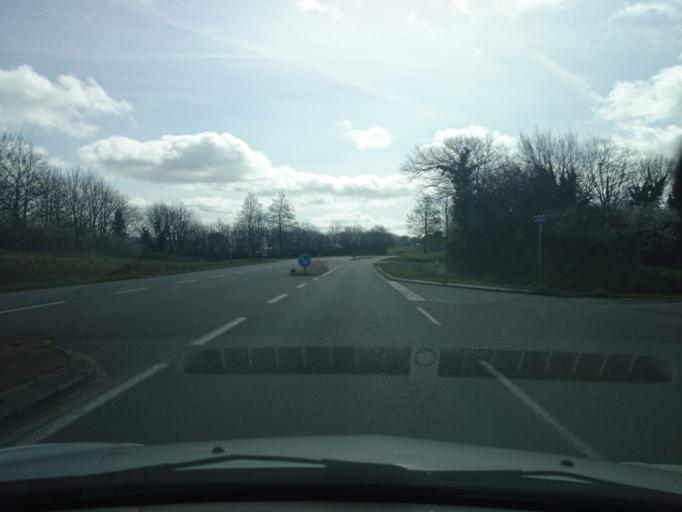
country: FR
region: Brittany
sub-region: Departement du Finistere
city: Gouesnou
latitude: 48.4357
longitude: -4.4454
